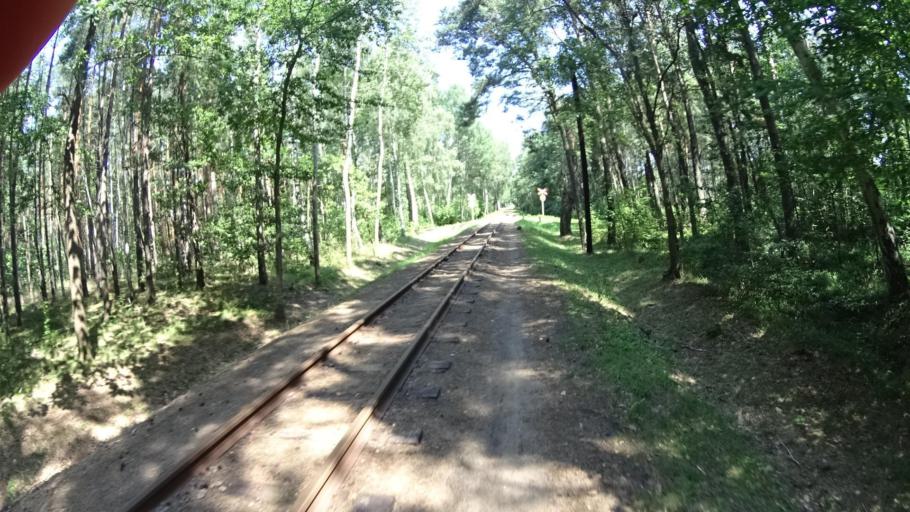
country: PL
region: Masovian Voivodeship
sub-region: Powiat piaseczynski
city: Lesznowola
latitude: 52.0157
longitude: 20.9289
